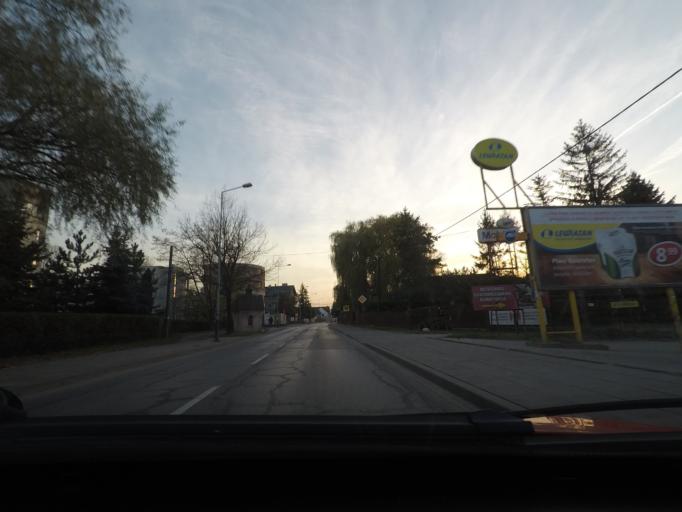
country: PL
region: Lesser Poland Voivodeship
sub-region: Krakow
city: Krakow
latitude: 50.0228
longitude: 19.9100
